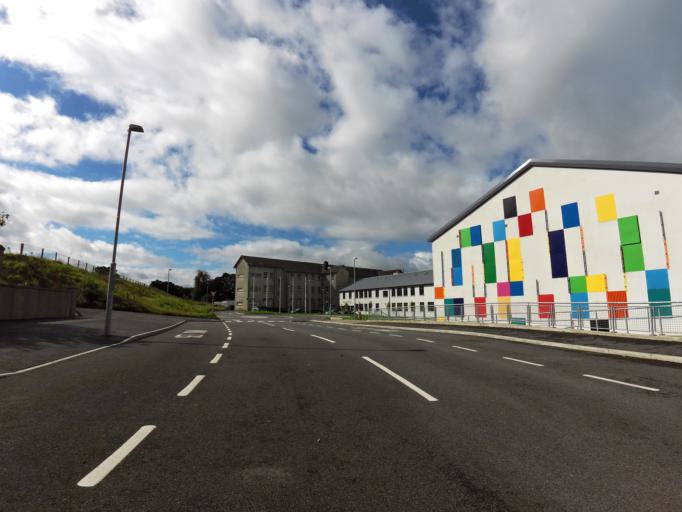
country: IE
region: Connaught
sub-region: County Galway
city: Loughrea
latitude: 53.1987
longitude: -8.5618
